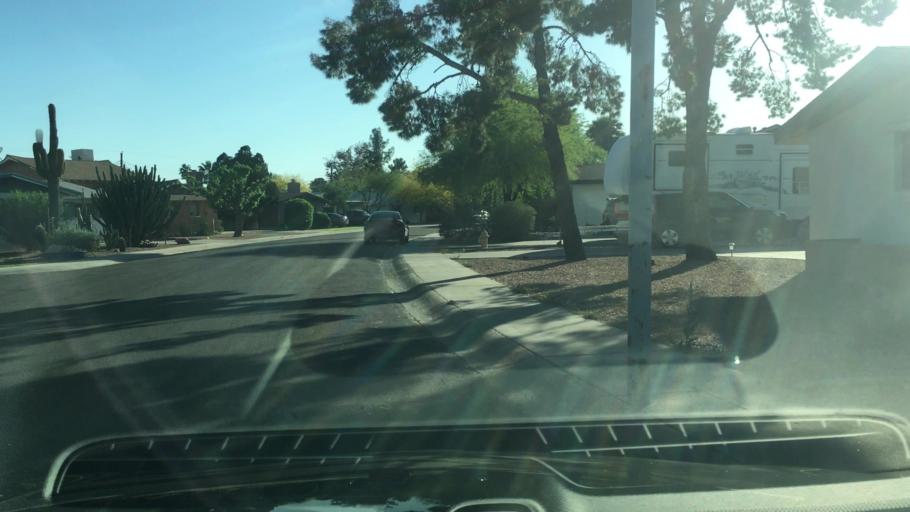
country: US
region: Arizona
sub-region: Maricopa County
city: Scottsdale
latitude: 33.5214
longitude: -111.8935
